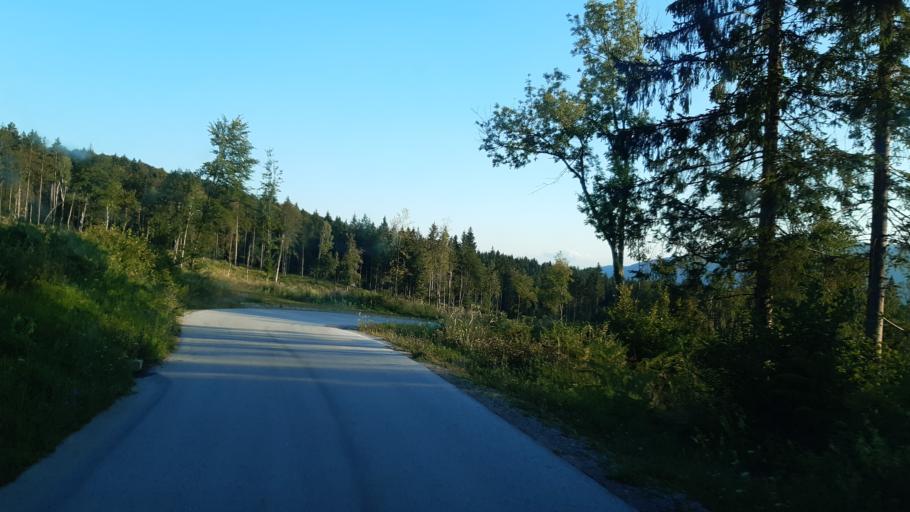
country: SI
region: Kocevje
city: Kocevje
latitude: 45.6575
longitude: 14.9048
